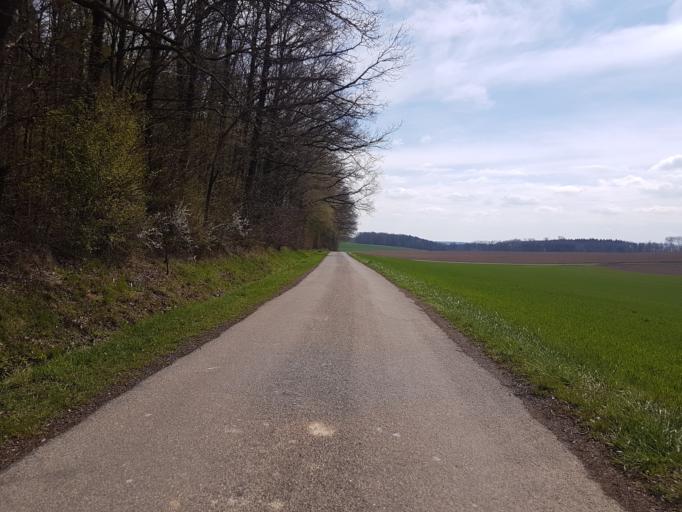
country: DE
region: Baden-Wuerttemberg
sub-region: Regierungsbezirk Stuttgart
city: Jagsthausen
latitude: 49.3747
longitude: 9.5221
